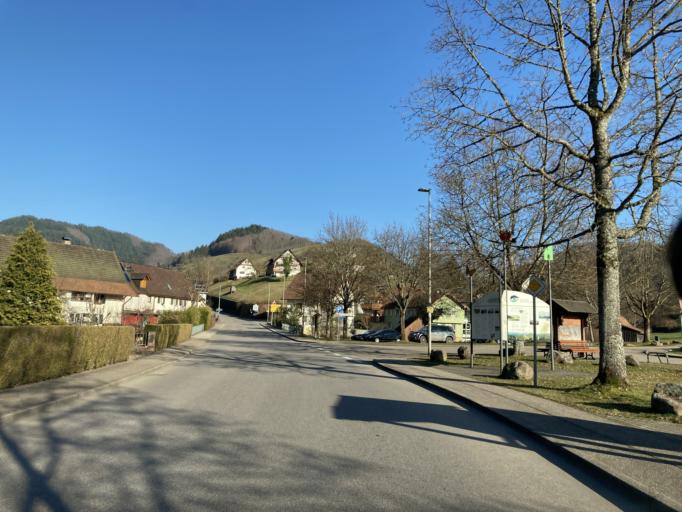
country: DE
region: Baden-Wuerttemberg
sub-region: Freiburg Region
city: Oppenau
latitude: 48.4772
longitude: 8.1718
